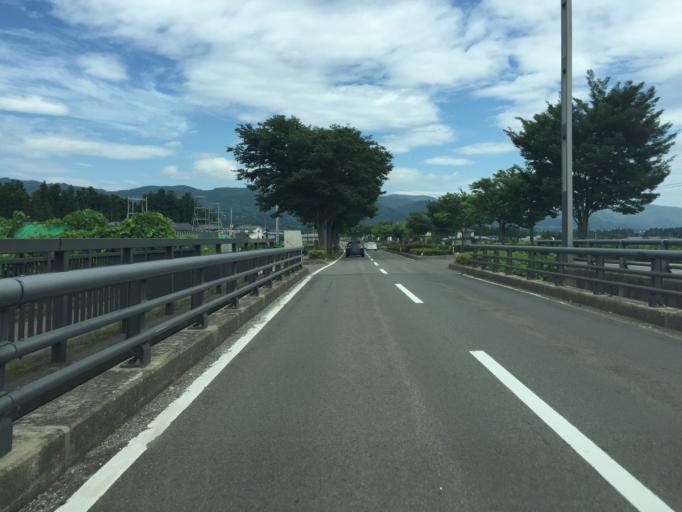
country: JP
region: Fukushima
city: Fukushima-shi
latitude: 37.7523
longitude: 140.3798
